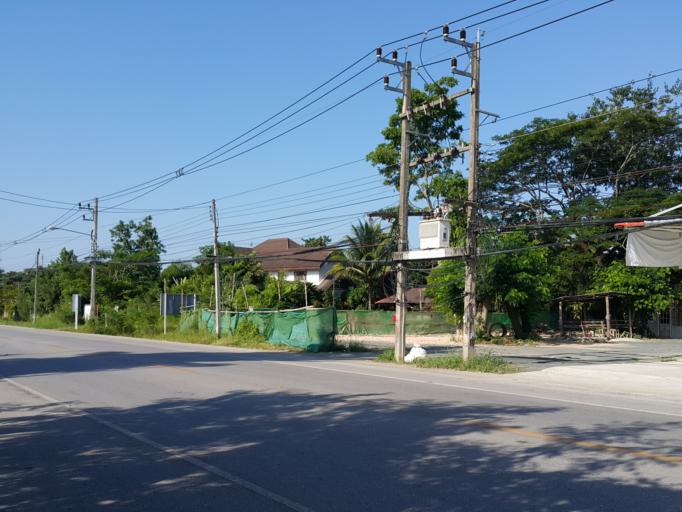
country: TH
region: Chiang Mai
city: San Kamphaeng
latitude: 18.7866
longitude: 99.0972
